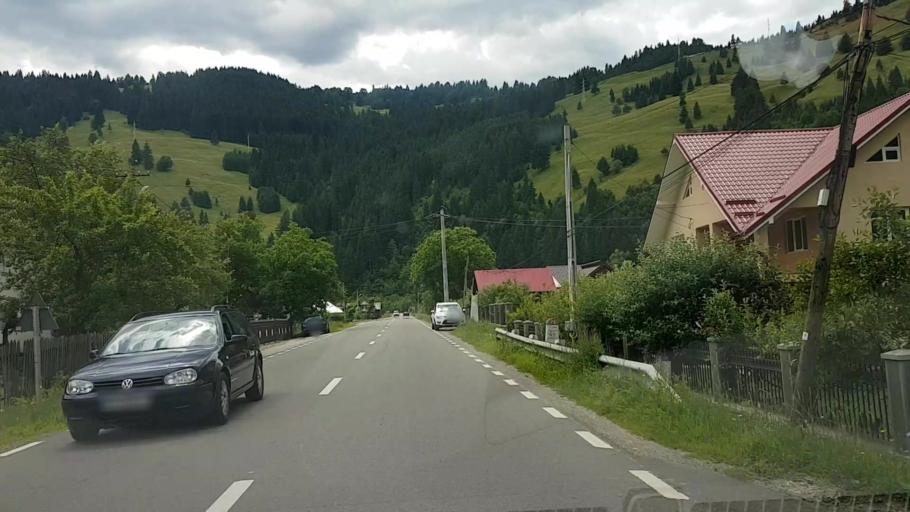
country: RO
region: Neamt
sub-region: Comuna Farcasa
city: Farcasa
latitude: 47.1439
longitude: 25.8626
